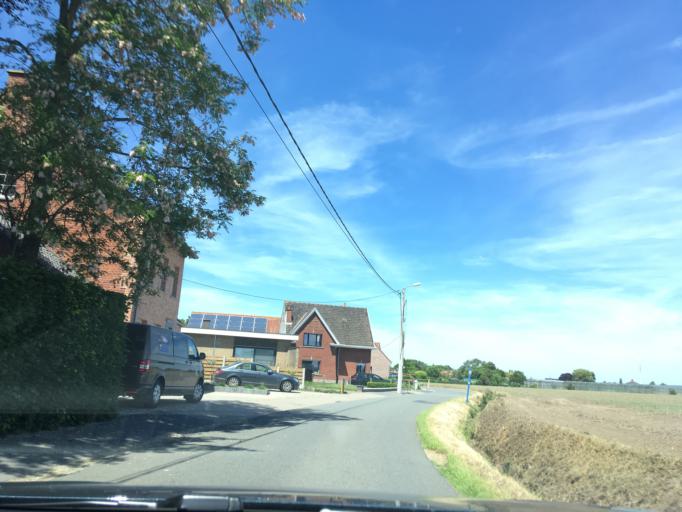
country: BE
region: Flanders
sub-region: Provincie West-Vlaanderen
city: Hooglede
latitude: 51.0032
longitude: 3.0969
